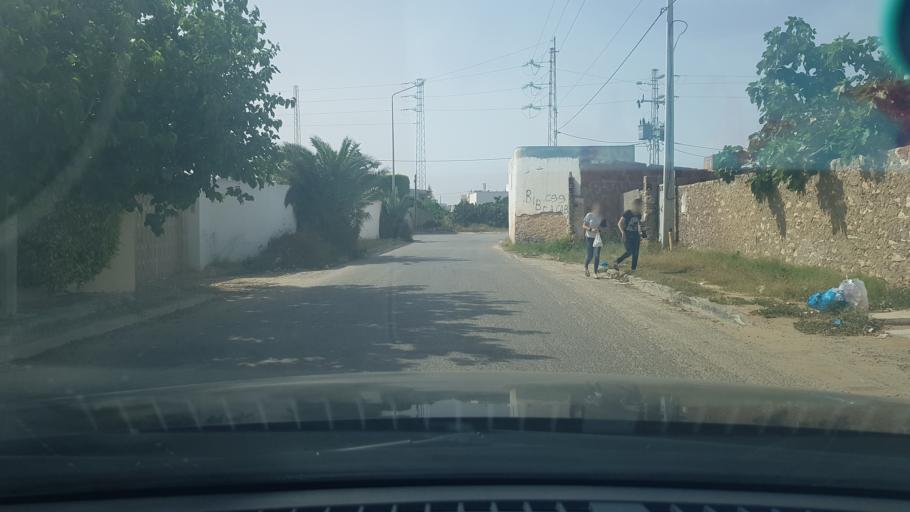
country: TN
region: Safaqis
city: Al Qarmadah
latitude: 34.8065
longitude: 10.7668
